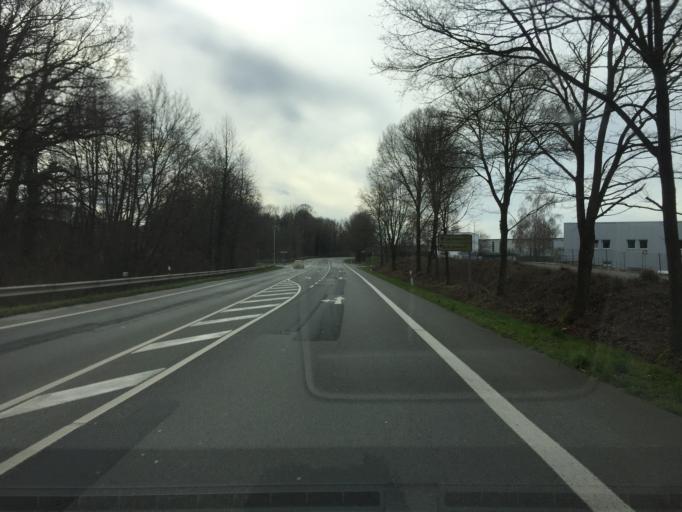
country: DE
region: North Rhine-Westphalia
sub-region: Regierungsbezirk Detmold
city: Vlotho
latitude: 52.1391
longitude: 8.8310
